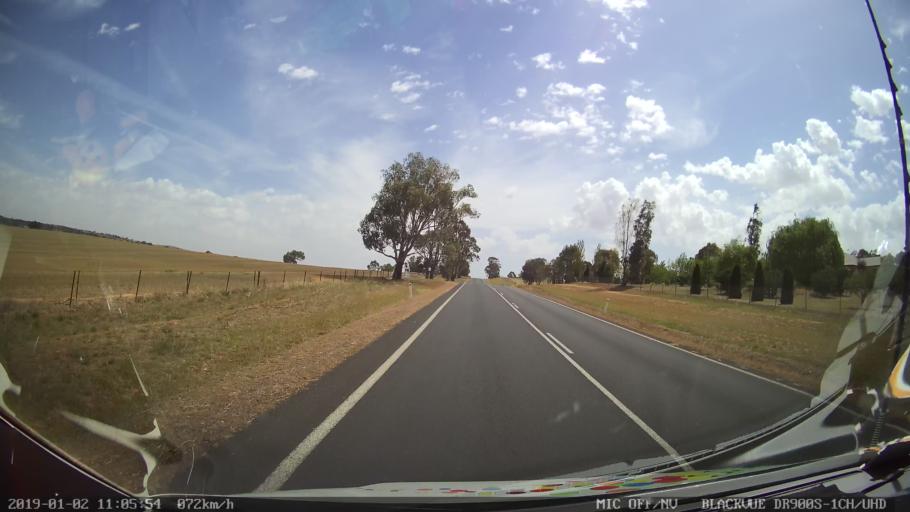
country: AU
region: New South Wales
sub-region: Young
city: Young
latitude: -34.5597
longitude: 148.3546
